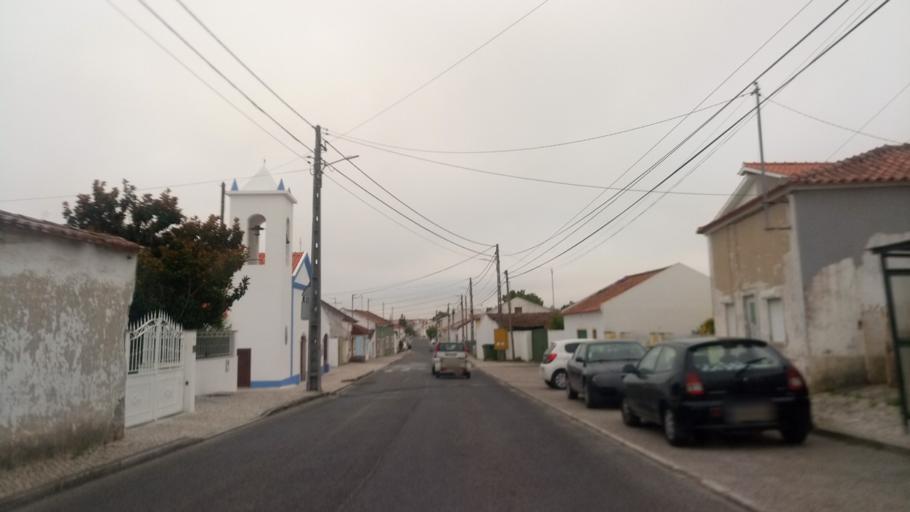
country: PT
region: Leiria
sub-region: Caldas da Rainha
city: Caldas da Rainha
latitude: 39.4358
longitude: -9.1530
